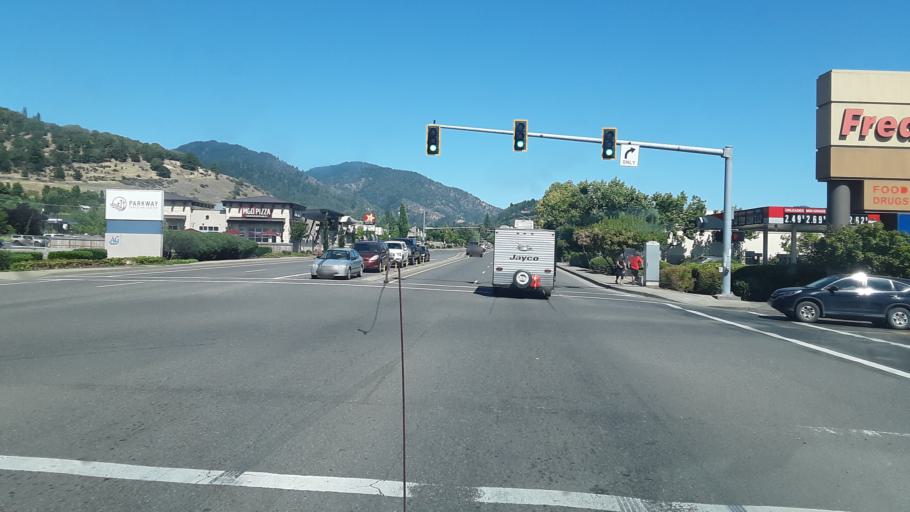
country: US
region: Oregon
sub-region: Josephine County
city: Fruitdale
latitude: 42.4368
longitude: -123.3056
